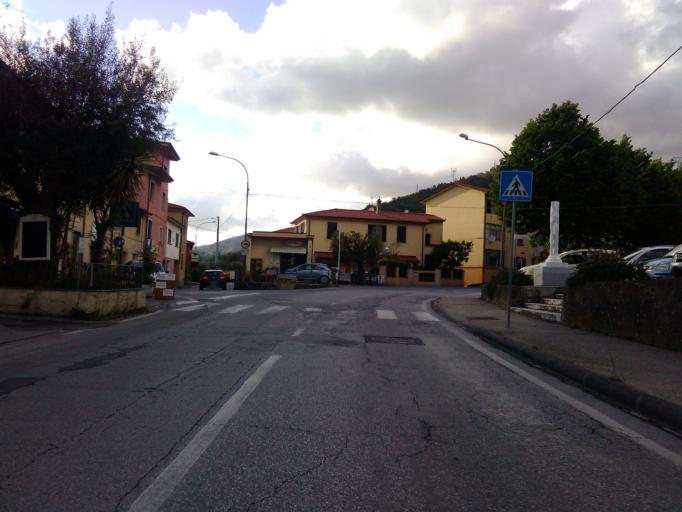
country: IT
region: Tuscany
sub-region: Provincia di Lucca
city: Seravezza
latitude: 43.9817
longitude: 10.2198
